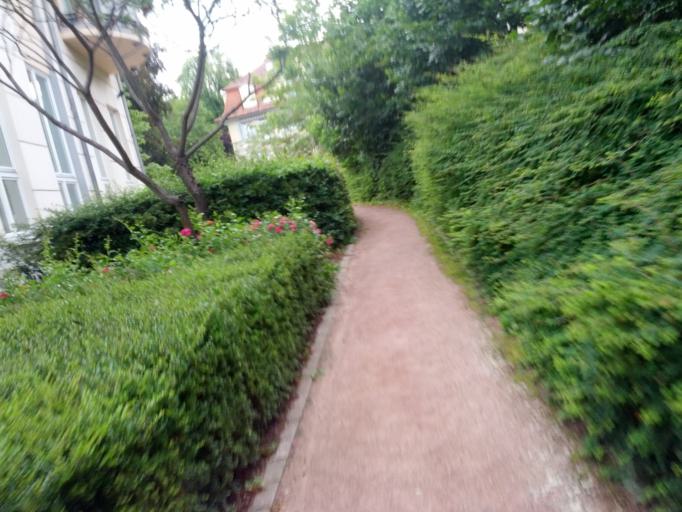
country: DE
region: Thuringia
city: Eisenach
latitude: 50.9713
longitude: 10.3249
